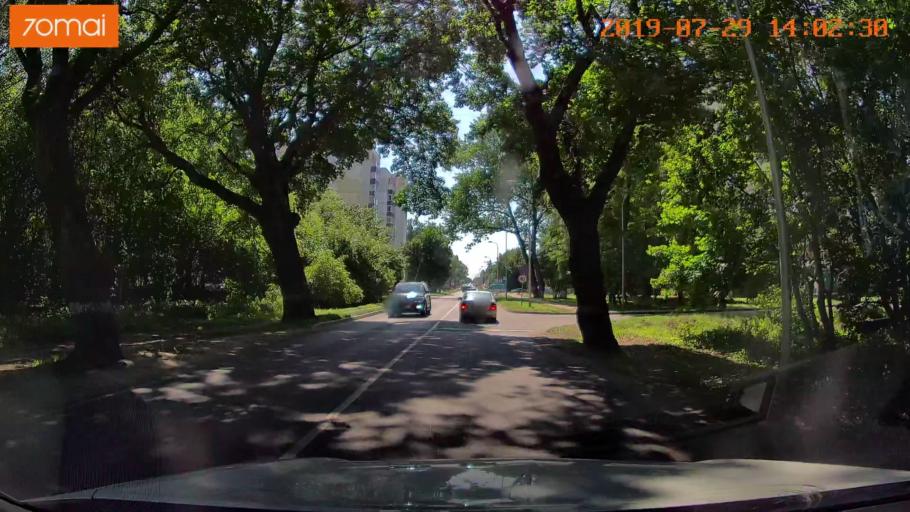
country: RU
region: Kaliningrad
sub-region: Gorod Kaliningrad
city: Baltiysk
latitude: 54.6626
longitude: 19.9158
